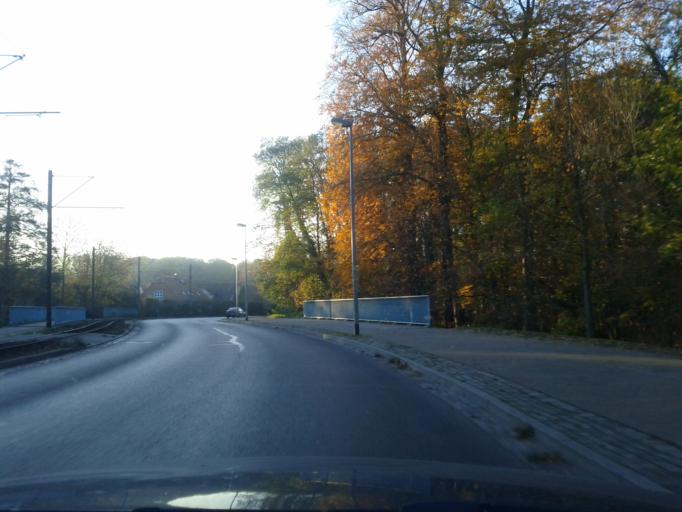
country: DE
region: Brandenburg
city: Schoneiche
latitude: 52.4791
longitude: 13.6985
